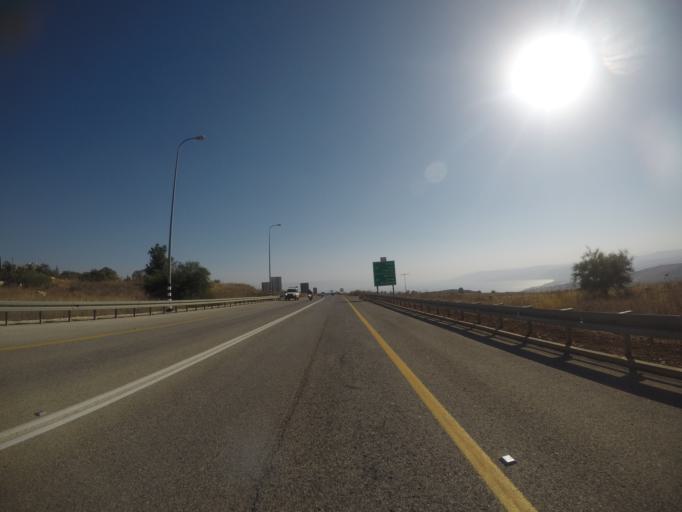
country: IL
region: Northern District
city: Rosh Pinna
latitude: 32.9119
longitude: 35.5454
